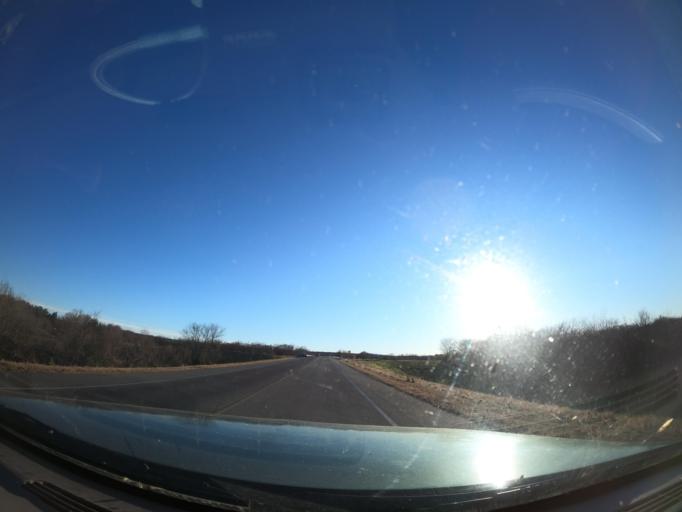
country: US
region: Oklahoma
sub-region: Pittsburg County
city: Hartshorne
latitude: 34.8492
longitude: -95.5366
